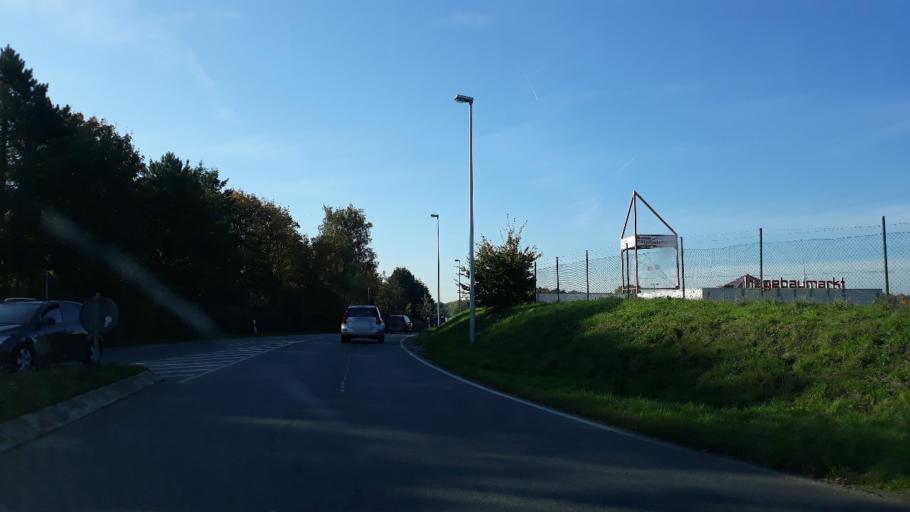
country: DE
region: Schleswig-Holstein
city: Schleswig
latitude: 54.5346
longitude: 9.5593
